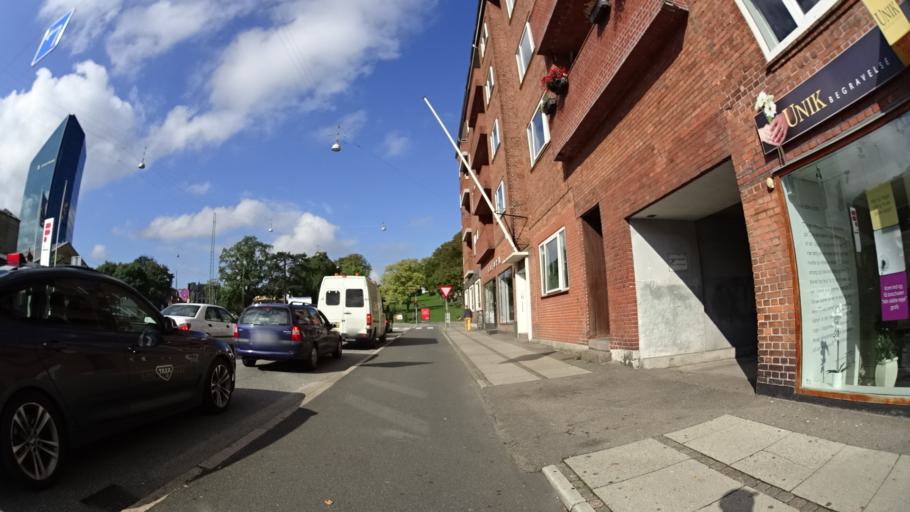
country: DK
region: Central Jutland
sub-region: Arhus Kommune
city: Arhus
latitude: 56.1571
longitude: 10.1951
